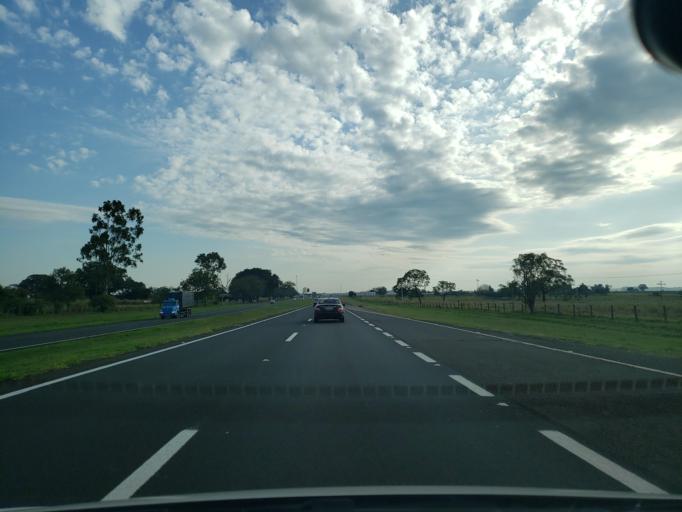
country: BR
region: Sao Paulo
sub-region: Guararapes
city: Guararapes
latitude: -21.2046
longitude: -50.6201
